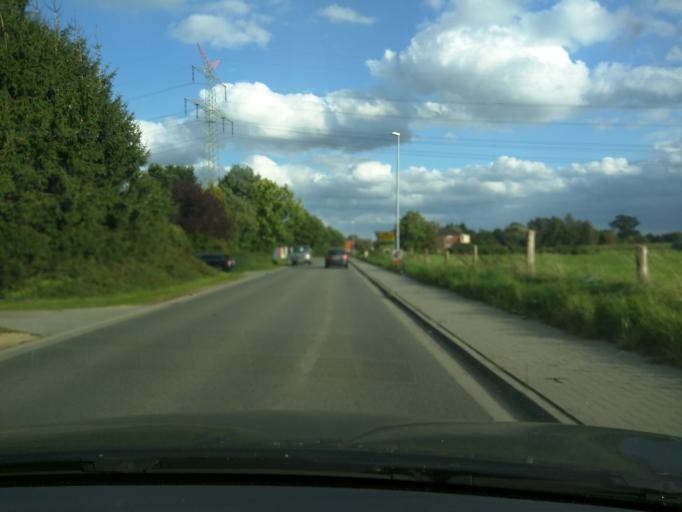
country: DE
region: Lower Saxony
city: Tespe
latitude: 53.4059
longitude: 10.4043
